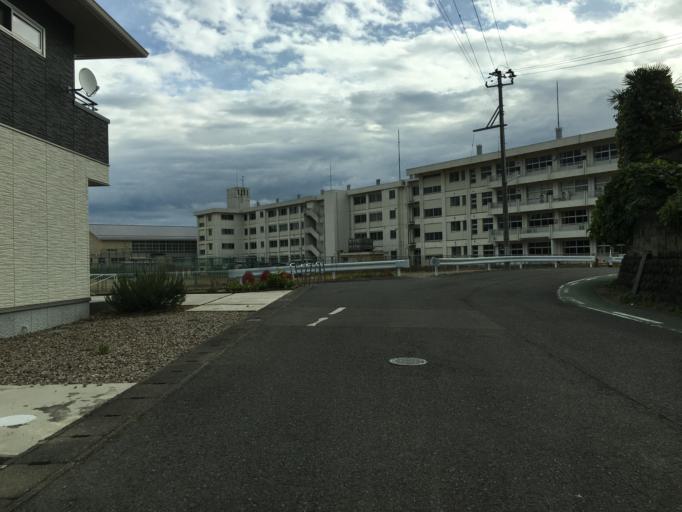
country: JP
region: Fukushima
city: Nihommatsu
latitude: 37.6024
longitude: 140.4391
